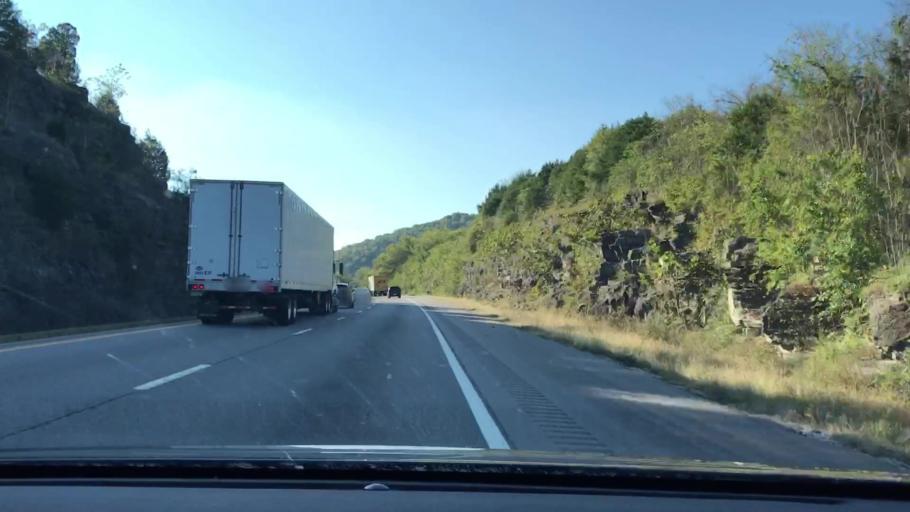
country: US
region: Tennessee
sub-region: Smith County
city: Gordonsville
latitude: 36.1458
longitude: -85.8504
